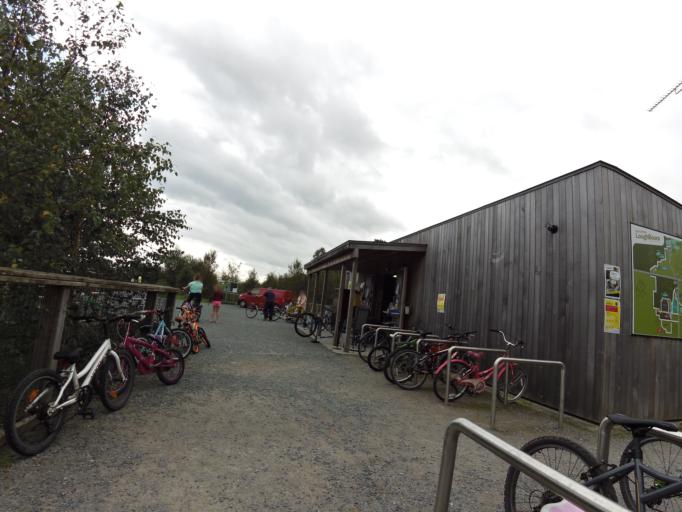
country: IE
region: Leinster
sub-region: Uibh Fhaili
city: Ferbane
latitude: 53.2228
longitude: -7.7289
